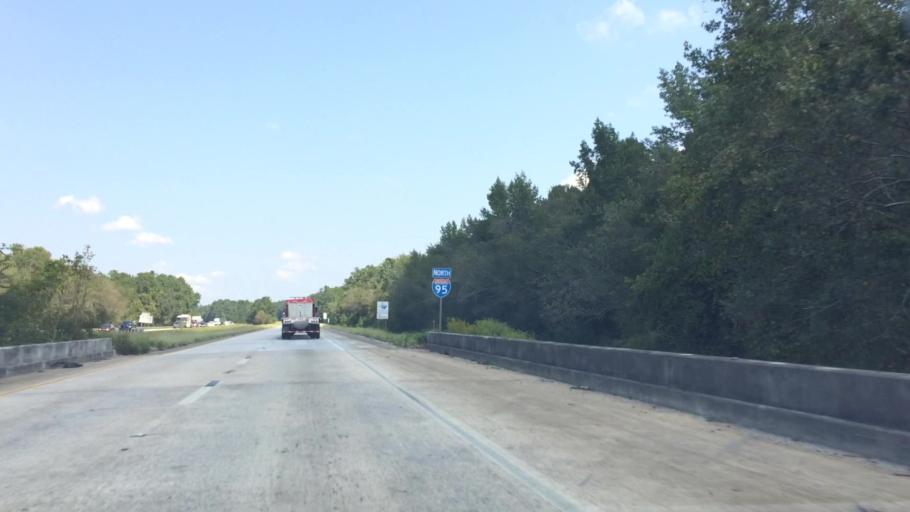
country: US
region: South Carolina
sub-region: Dorchester County
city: Saint George
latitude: 33.0912
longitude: -80.6492
